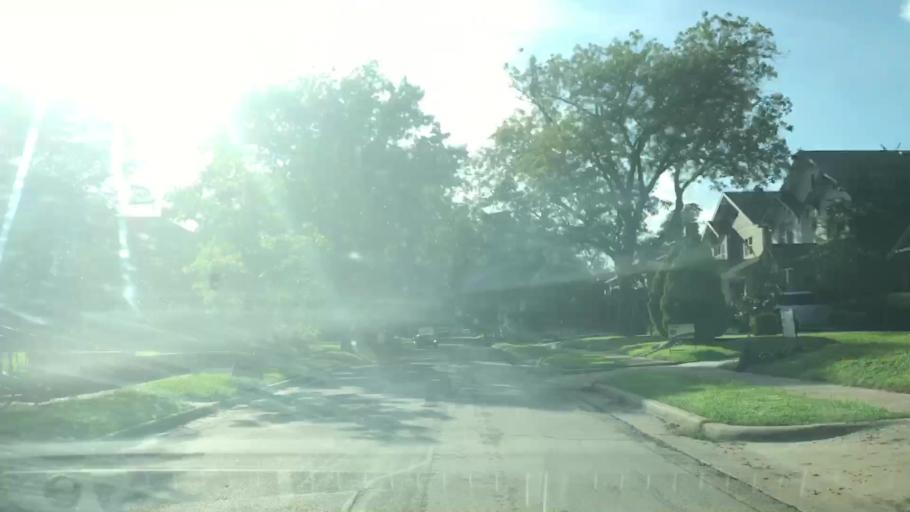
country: US
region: Texas
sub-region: Dallas County
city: Highland Park
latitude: 32.8213
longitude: -96.7747
